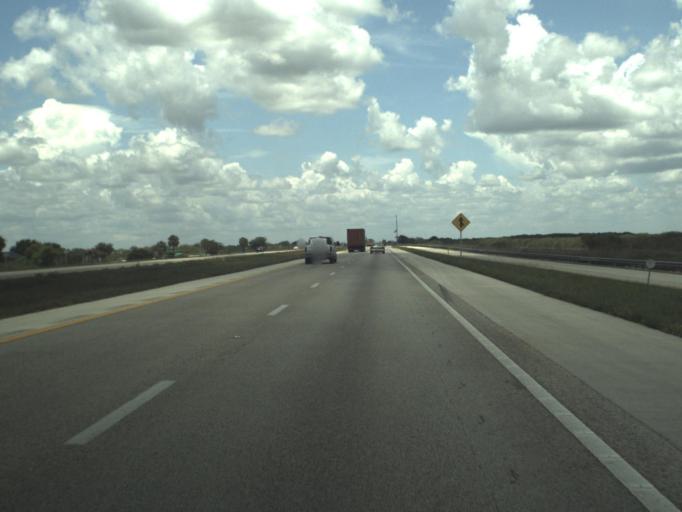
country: US
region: Florida
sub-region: Broward County
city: Weston
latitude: 26.1465
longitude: -80.5756
